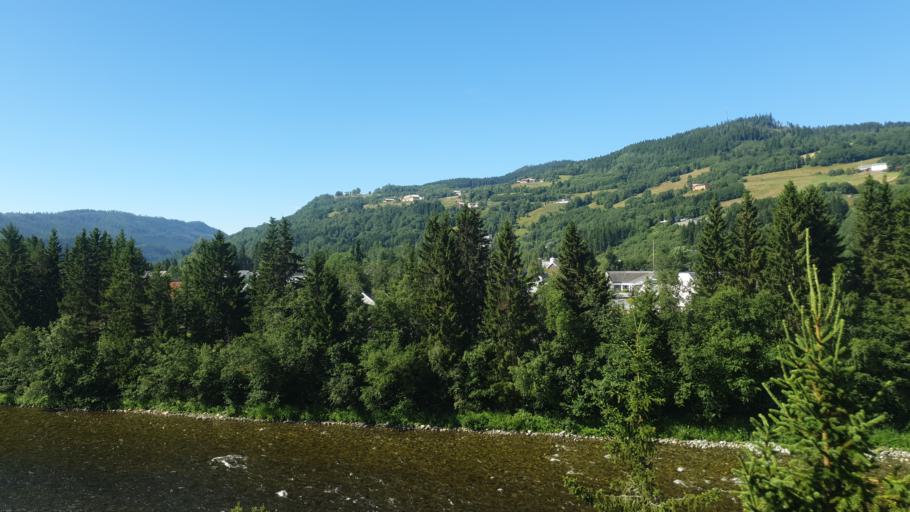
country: NO
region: Sor-Trondelag
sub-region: Meldal
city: Meldal
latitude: 63.1711
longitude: 9.7488
